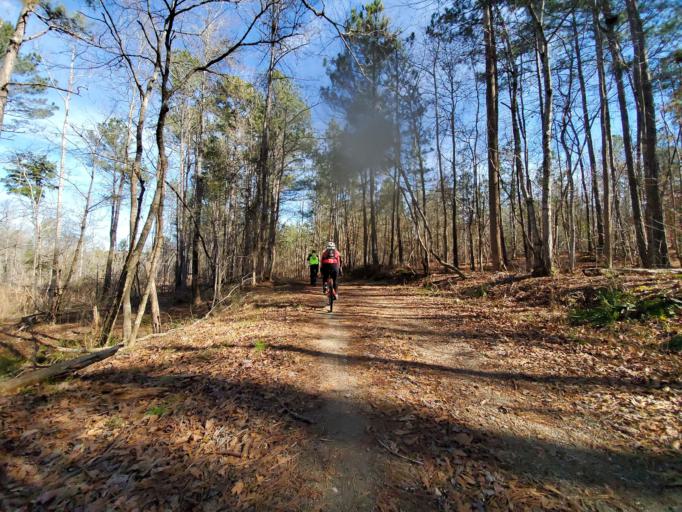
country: US
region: Georgia
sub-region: Fulton County
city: Chattahoochee Hills
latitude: 33.5710
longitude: -84.7349
